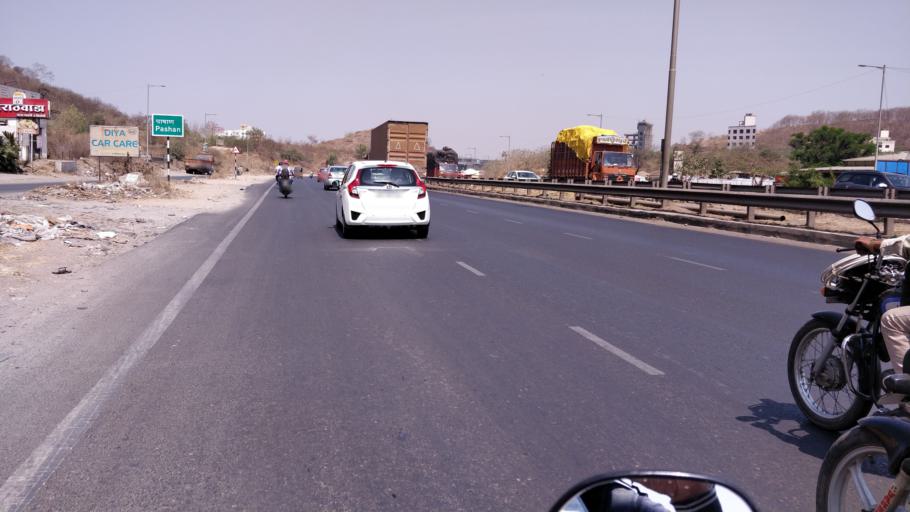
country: IN
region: Maharashtra
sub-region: Pune Division
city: Shivaji Nagar
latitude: 18.5433
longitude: 73.7759
